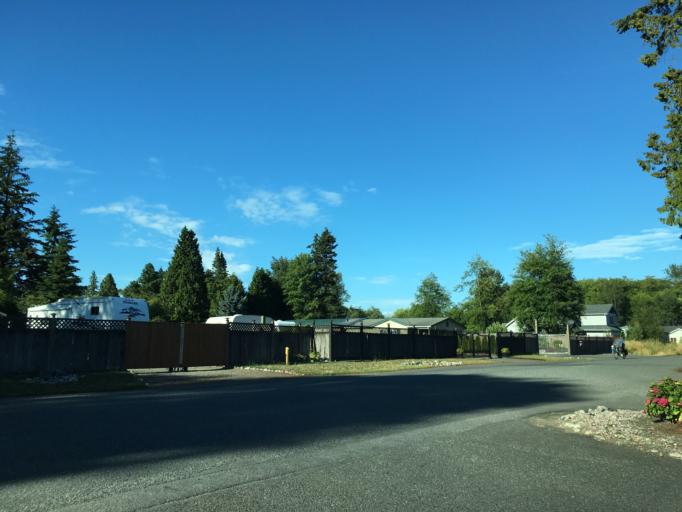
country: US
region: Washington
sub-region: Whatcom County
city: Birch Bay
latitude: 48.9068
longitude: -122.7538
